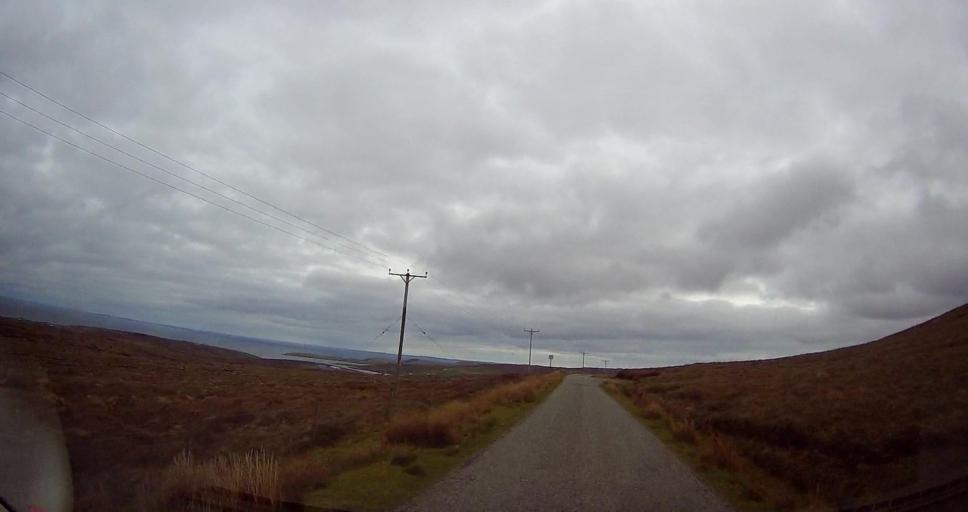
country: GB
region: Scotland
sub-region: Shetland Islands
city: Shetland
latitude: 60.5725
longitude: -1.0670
